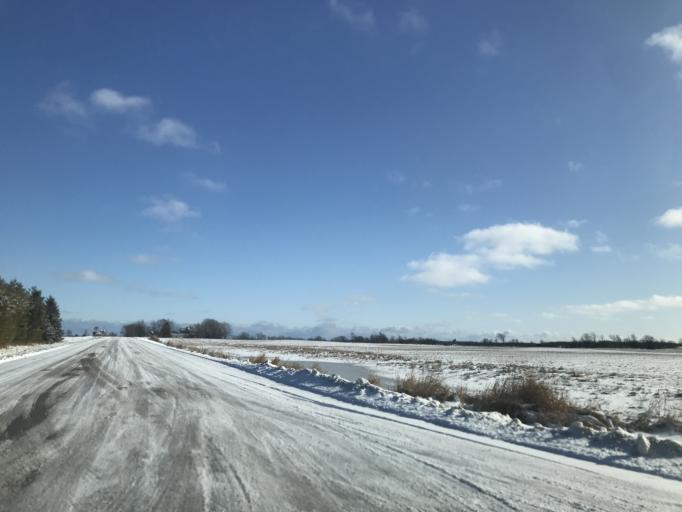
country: US
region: Wisconsin
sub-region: Kewaunee County
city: Luxemburg
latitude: 44.6977
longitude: -87.6203
